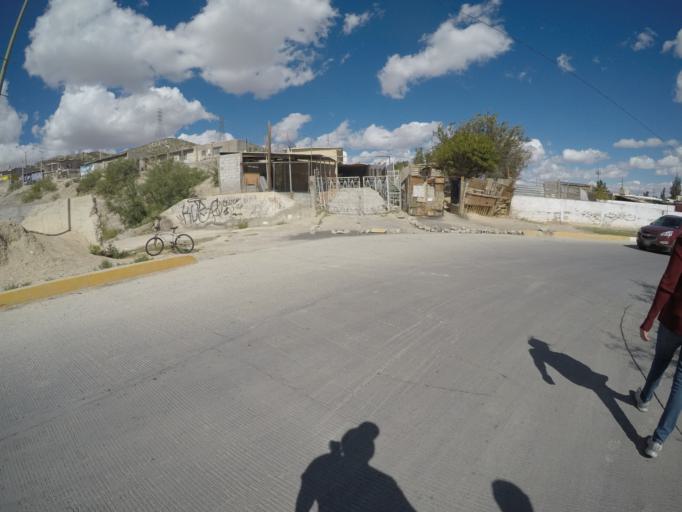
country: MX
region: Chihuahua
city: Ciudad Juarez
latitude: 31.6914
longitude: -106.4852
